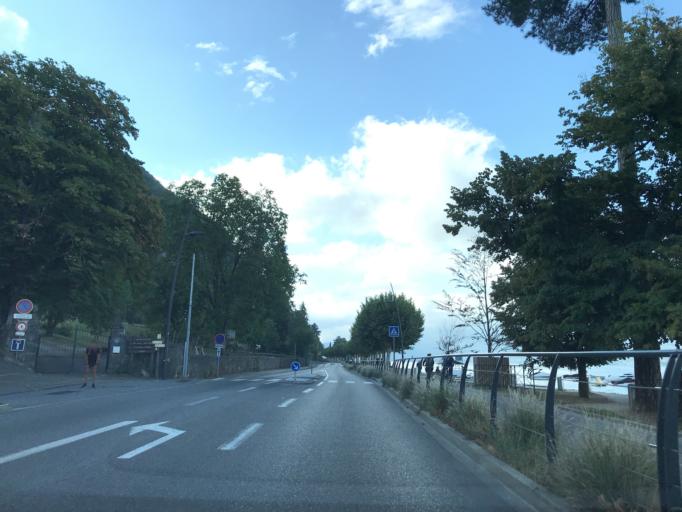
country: FR
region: Rhone-Alpes
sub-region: Departement de la Haute-Savoie
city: Annecy-le-Vieux
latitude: 45.9043
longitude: 6.1596
